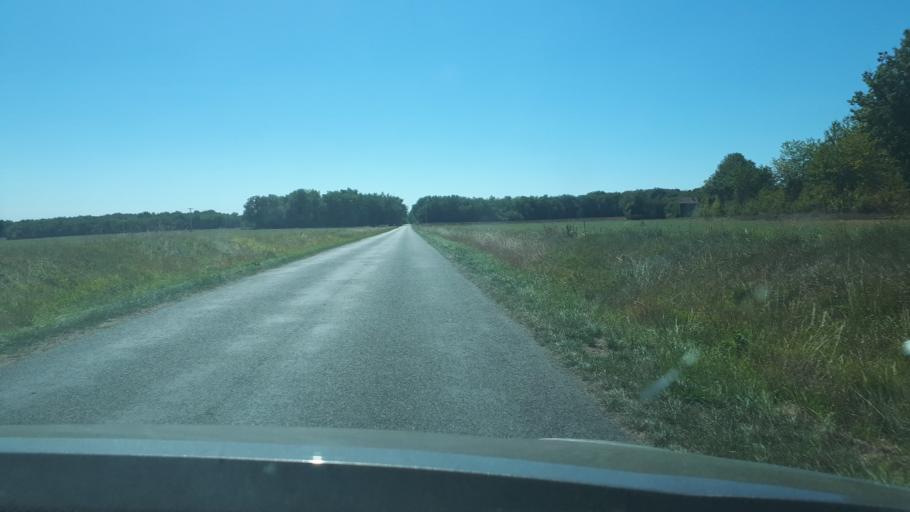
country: FR
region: Centre
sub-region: Departement du Cher
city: Sancerre
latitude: 47.2422
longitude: 2.7581
